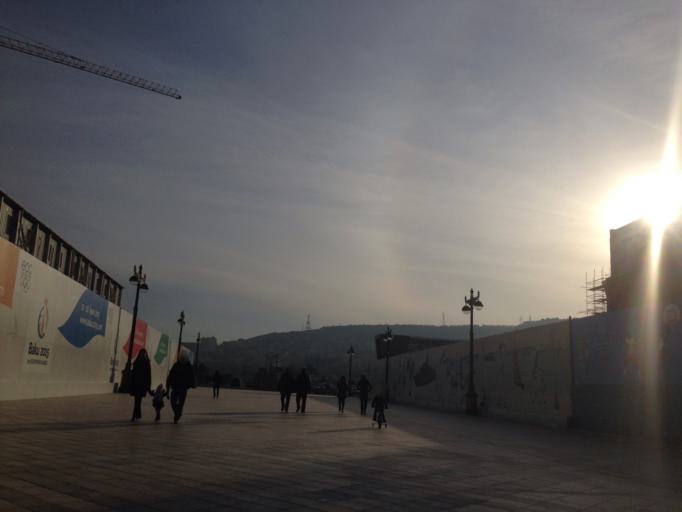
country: AZ
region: Baki
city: Badamdar
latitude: 40.3590
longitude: 49.8361
